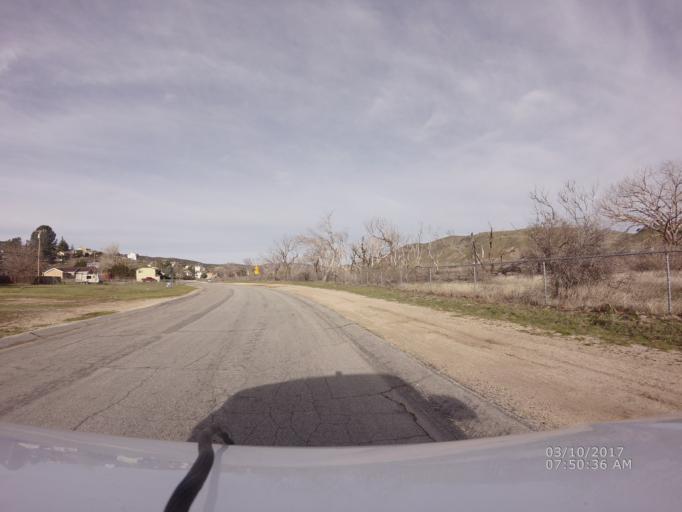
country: US
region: California
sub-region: Los Angeles County
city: Green Valley
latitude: 34.6623
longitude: -118.3919
